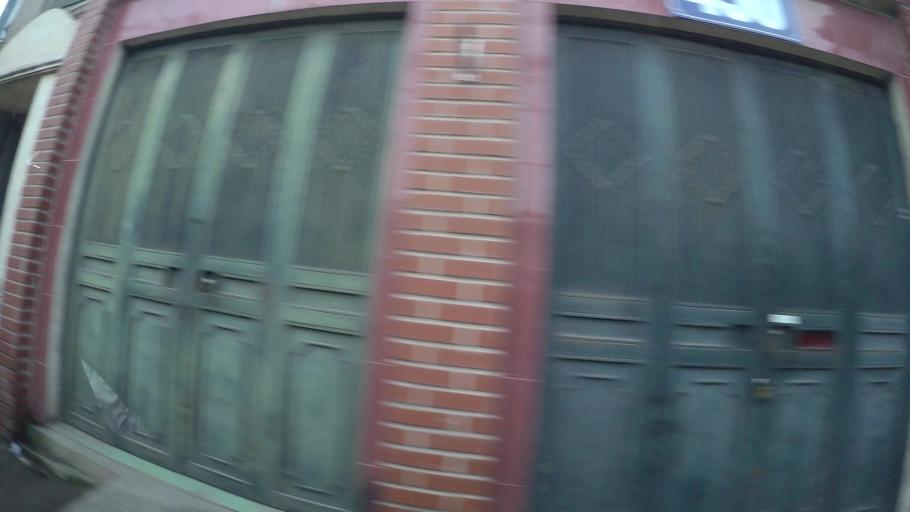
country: VN
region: Ha Noi
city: Hai BaTrung
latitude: 21.0019
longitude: 105.8762
